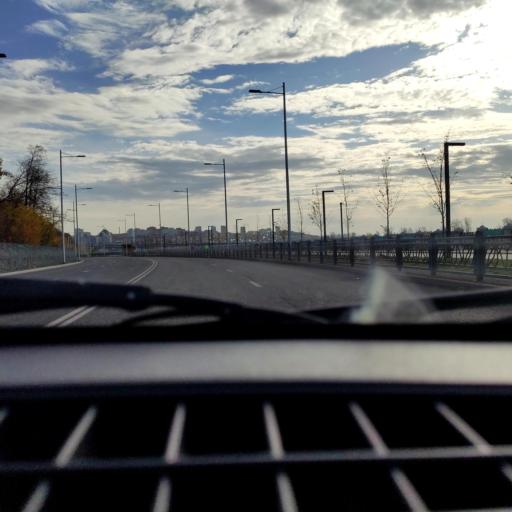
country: RU
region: Bashkortostan
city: Ufa
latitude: 54.7137
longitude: 55.9389
